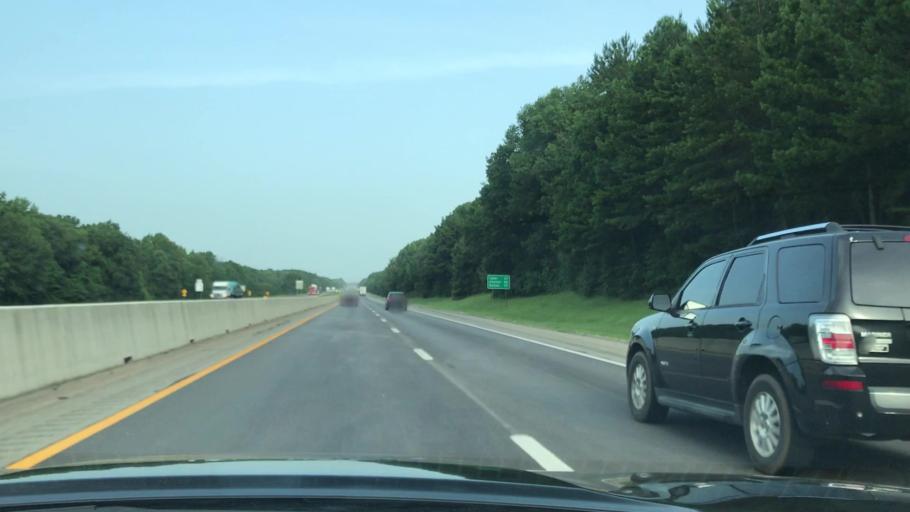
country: US
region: Texas
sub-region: Gregg County
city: Kilgore
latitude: 32.4326
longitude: -94.8742
